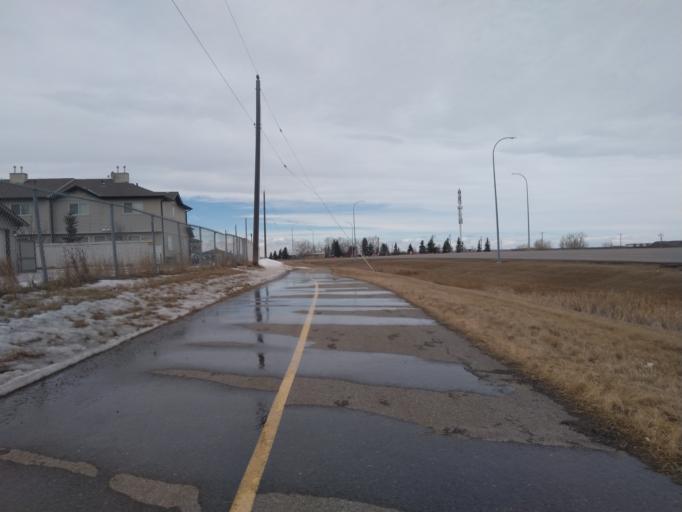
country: CA
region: Alberta
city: Chestermere
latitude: 51.1388
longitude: -113.9323
